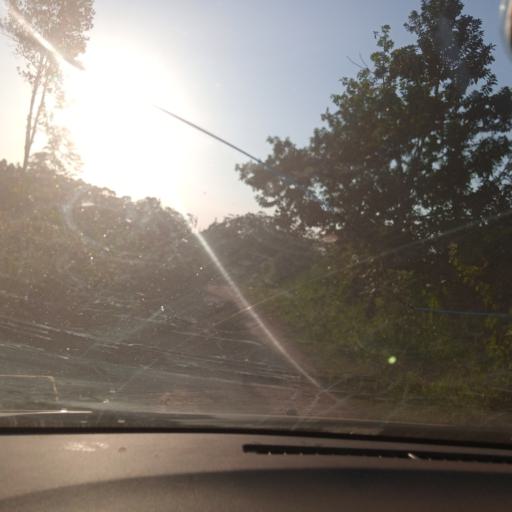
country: UG
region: Central Region
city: Masaka
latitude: -0.3414
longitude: 31.7585
